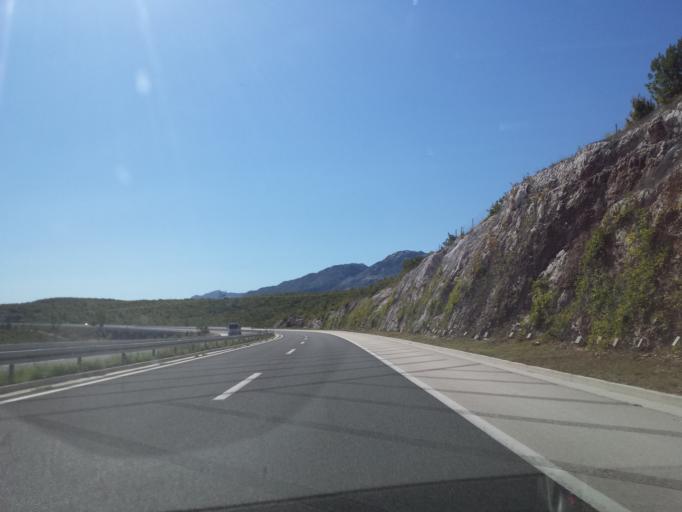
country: HR
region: Splitsko-Dalmatinska
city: Dugopolje
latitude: 43.5930
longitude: 16.6264
